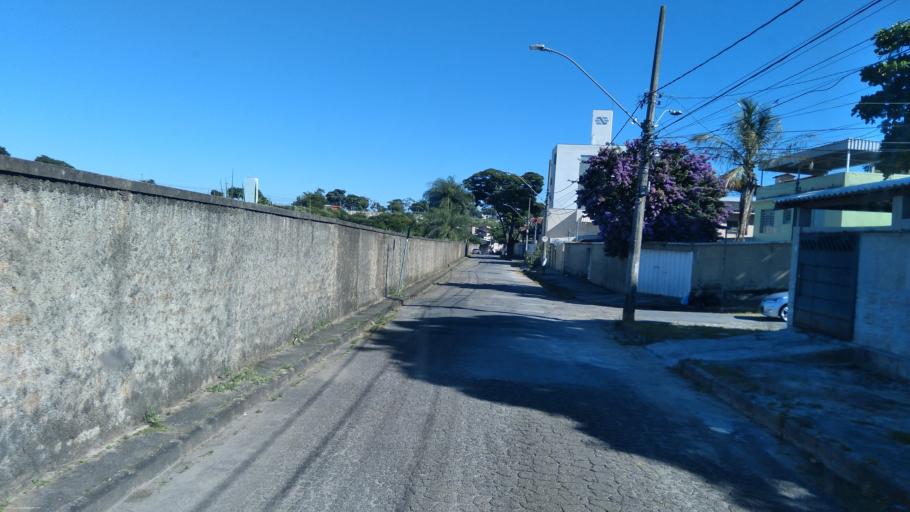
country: BR
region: Minas Gerais
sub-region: Belo Horizonte
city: Belo Horizonte
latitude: -19.8848
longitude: -43.9118
